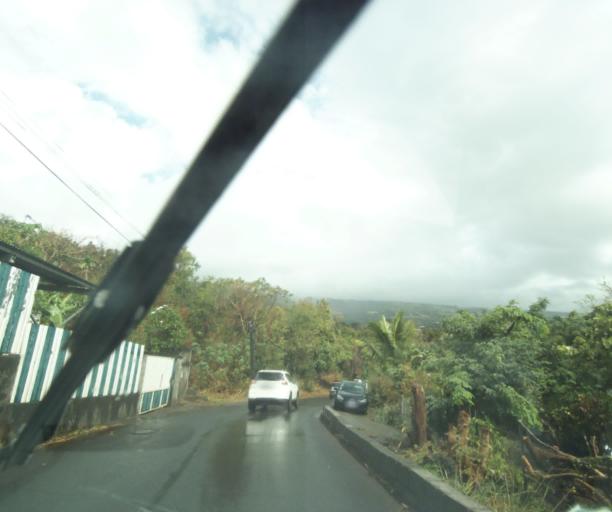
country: RE
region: Reunion
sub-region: Reunion
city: La Possession
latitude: -20.9752
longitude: 55.3309
